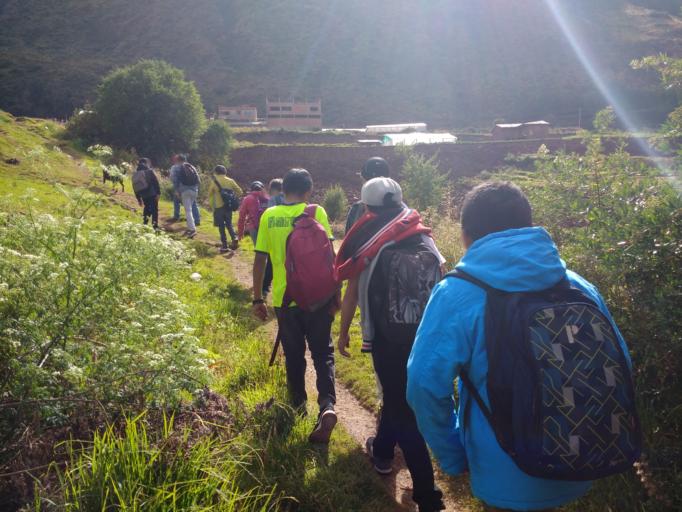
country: PE
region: Cusco
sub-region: Provincia de Cusco
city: Cusco
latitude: -13.5079
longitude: -71.9189
